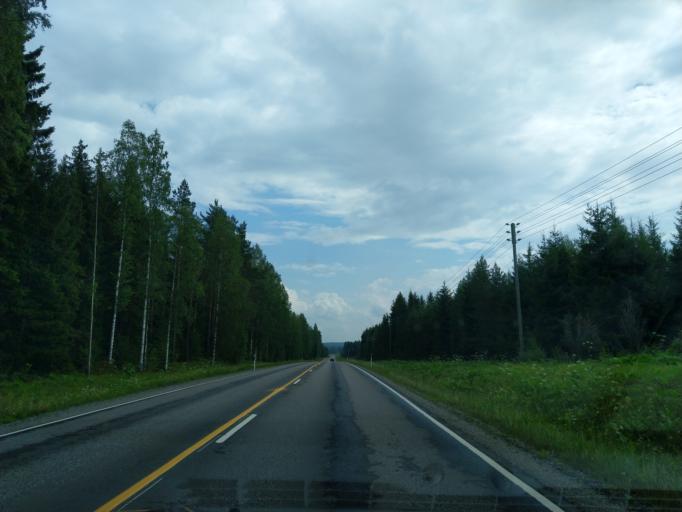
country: FI
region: South Karelia
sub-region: Imatra
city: Parikkala
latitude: 61.6160
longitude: 29.4474
